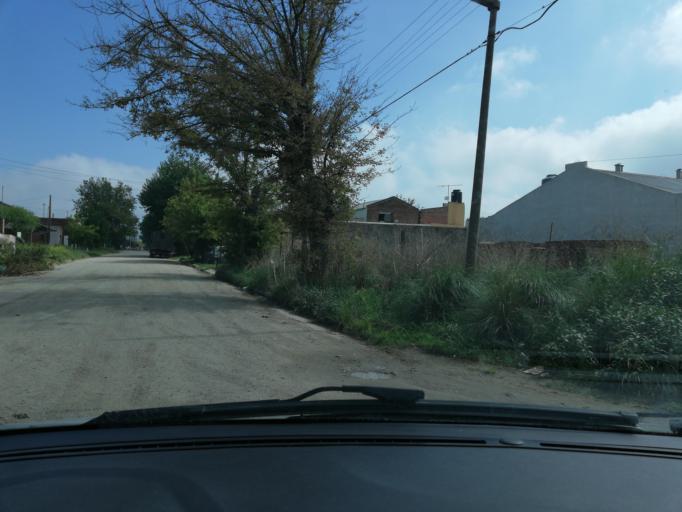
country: AR
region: Buenos Aires
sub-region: Partido de Balcarce
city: Balcarce
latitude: -37.8515
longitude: -58.2430
